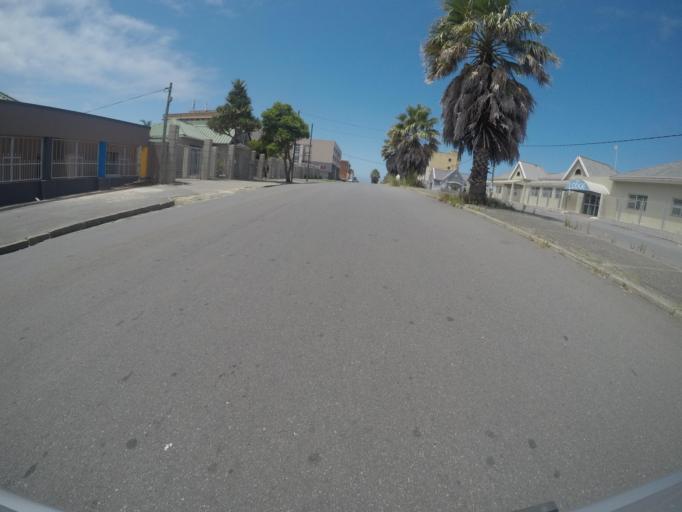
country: ZA
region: Eastern Cape
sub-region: Buffalo City Metropolitan Municipality
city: East London
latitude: -33.0187
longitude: 27.9117
